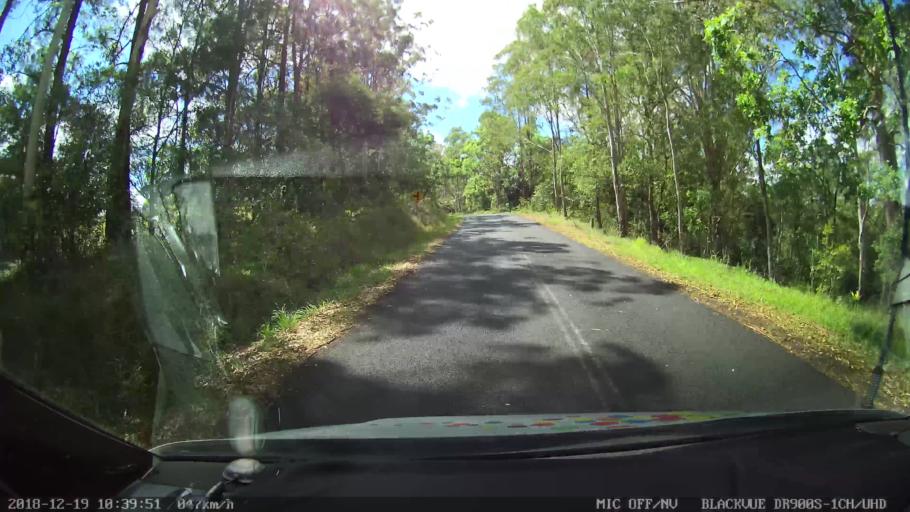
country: AU
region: New South Wales
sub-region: Lismore Municipality
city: Nimbin
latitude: -28.5826
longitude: 153.1570
